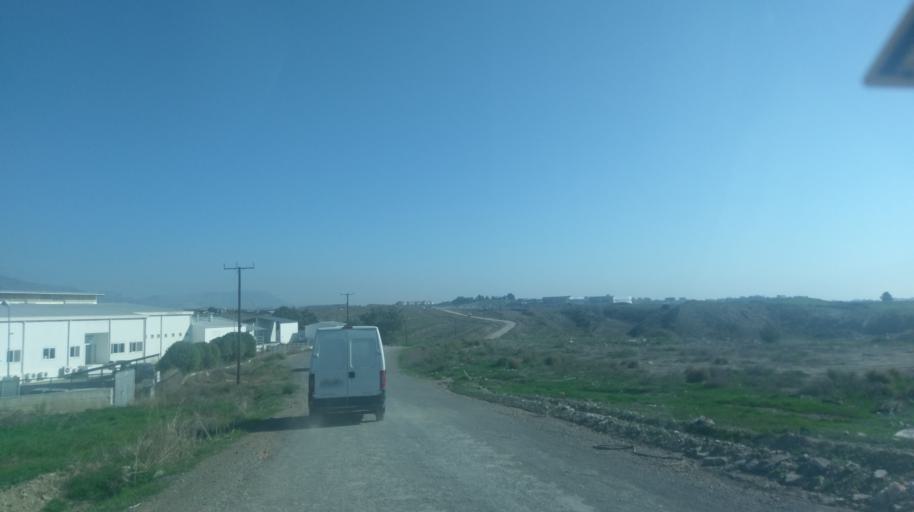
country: CY
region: Lefkosia
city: Nicosia
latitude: 35.2220
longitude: 33.3527
